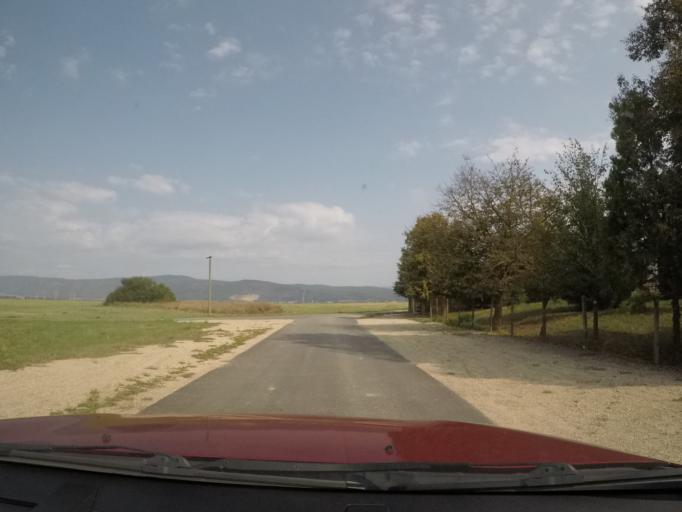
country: SK
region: Kosicky
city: Moldava nad Bodvou
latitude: 48.5809
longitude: 20.9551
